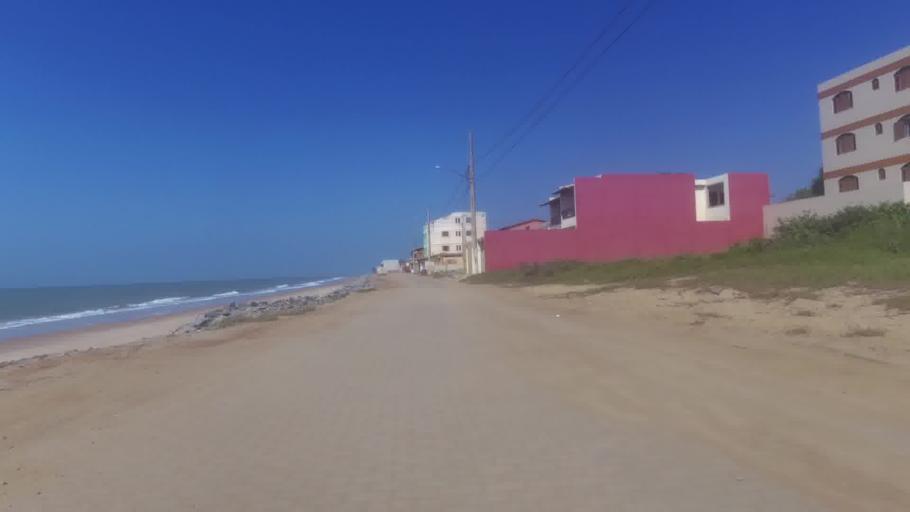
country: BR
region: Espirito Santo
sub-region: Marataizes
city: Marataizes
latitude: -21.0629
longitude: -40.8351
